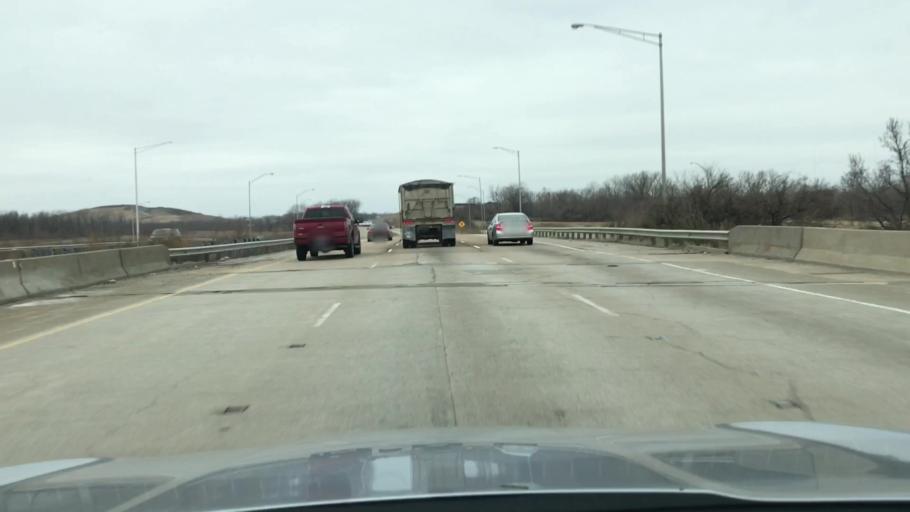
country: US
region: Illinois
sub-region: Saint Clair County
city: Fairmont City
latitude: 38.6629
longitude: -90.0933
